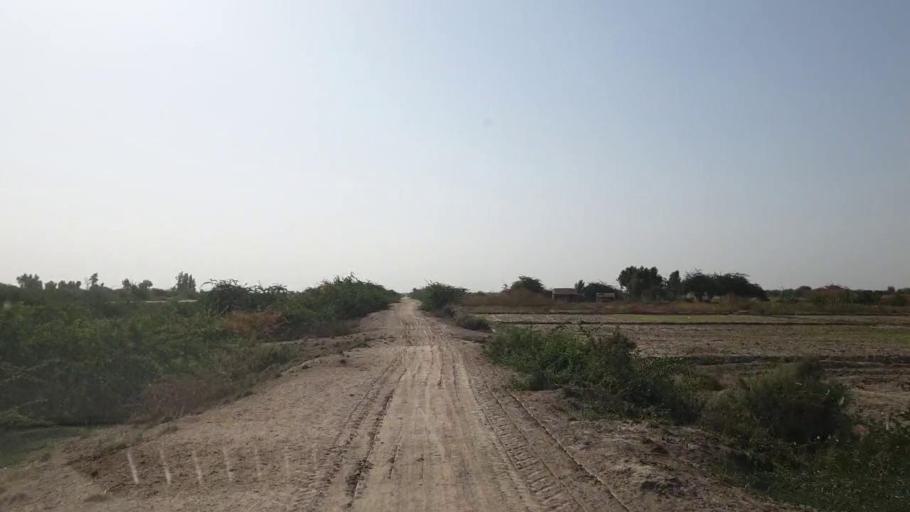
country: PK
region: Sindh
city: Kadhan
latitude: 24.5774
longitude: 69.0807
